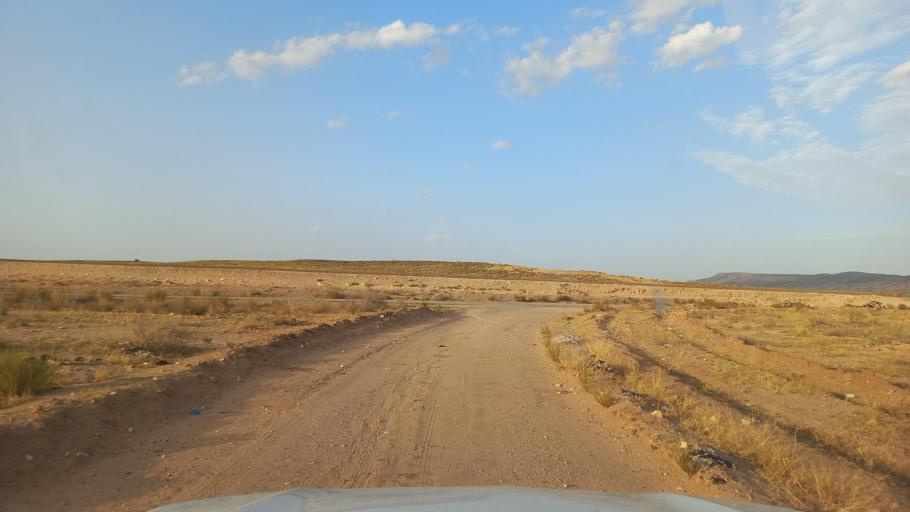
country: TN
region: Al Qasrayn
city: Sbiba
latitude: 35.3089
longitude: 9.0738
